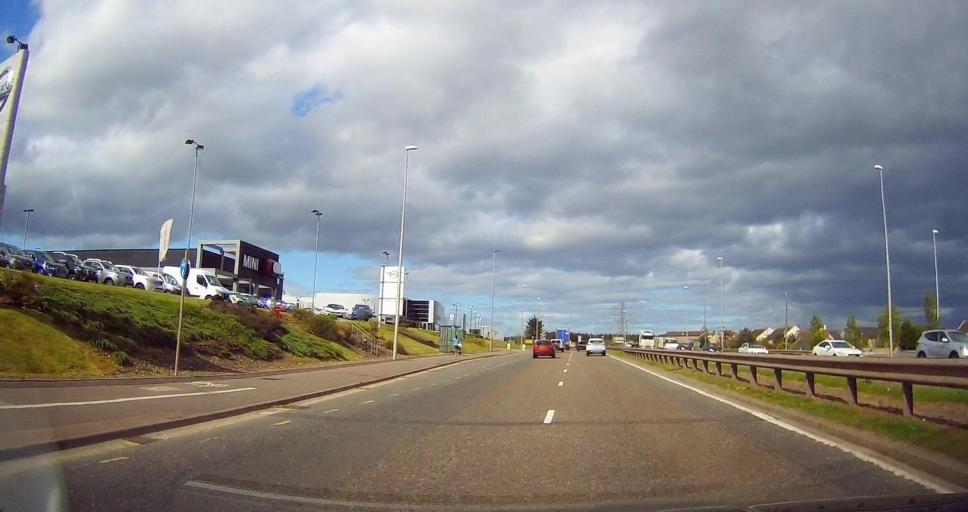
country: GB
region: Scotland
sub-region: Aberdeen City
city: Aberdeen
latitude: 57.1056
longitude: -2.0959
